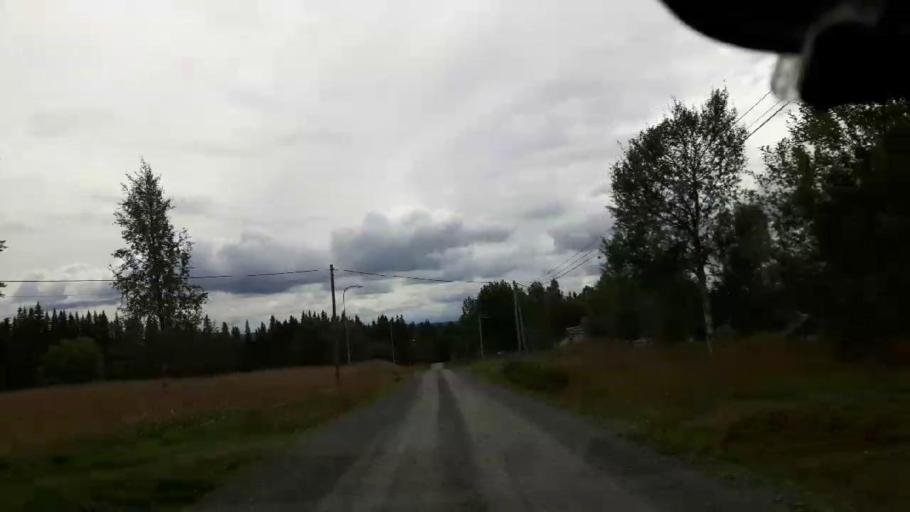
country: SE
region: Jaemtland
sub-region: Krokoms Kommun
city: Valla
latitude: 63.7002
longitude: 13.8728
